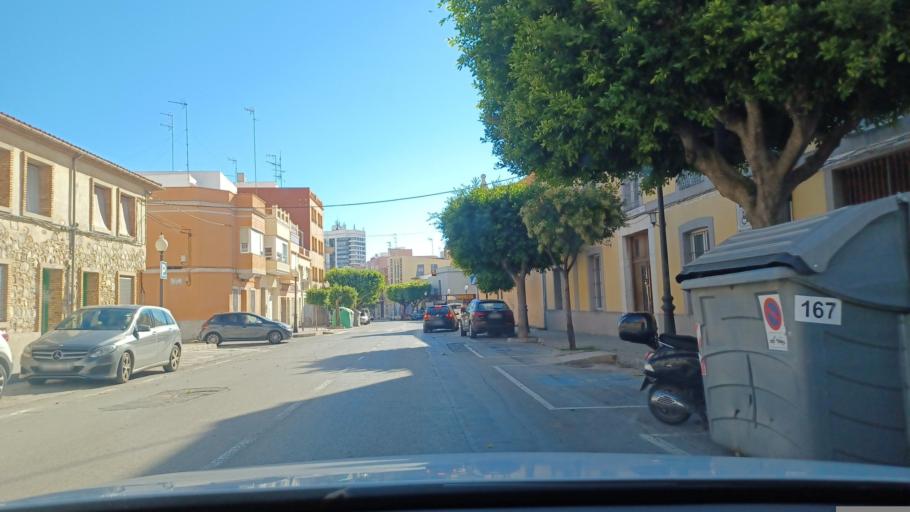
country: ES
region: Valencia
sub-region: Provincia de Castello
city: Benicarlo
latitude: 40.4207
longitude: 0.4201
